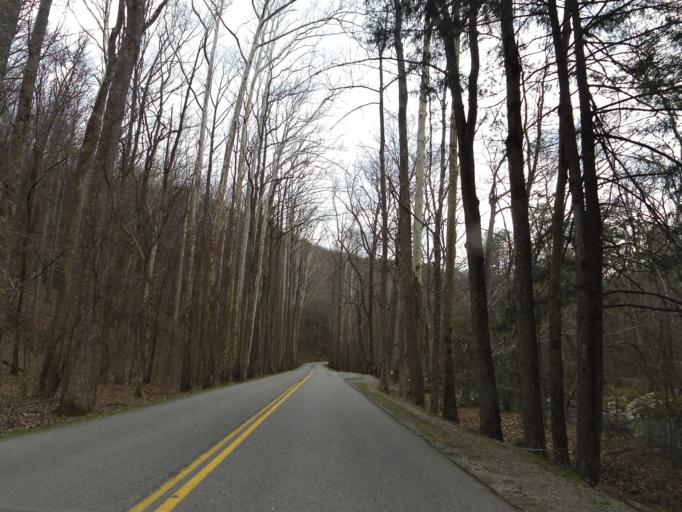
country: US
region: Tennessee
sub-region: Sevier County
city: Gatlinburg
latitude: 35.6724
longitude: -83.6413
